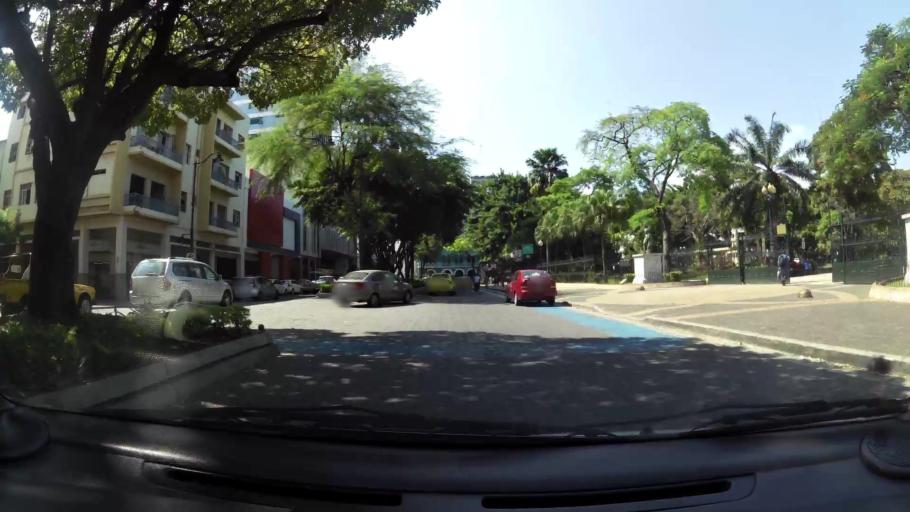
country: EC
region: Guayas
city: Guayaquil
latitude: -2.1890
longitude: -79.8878
